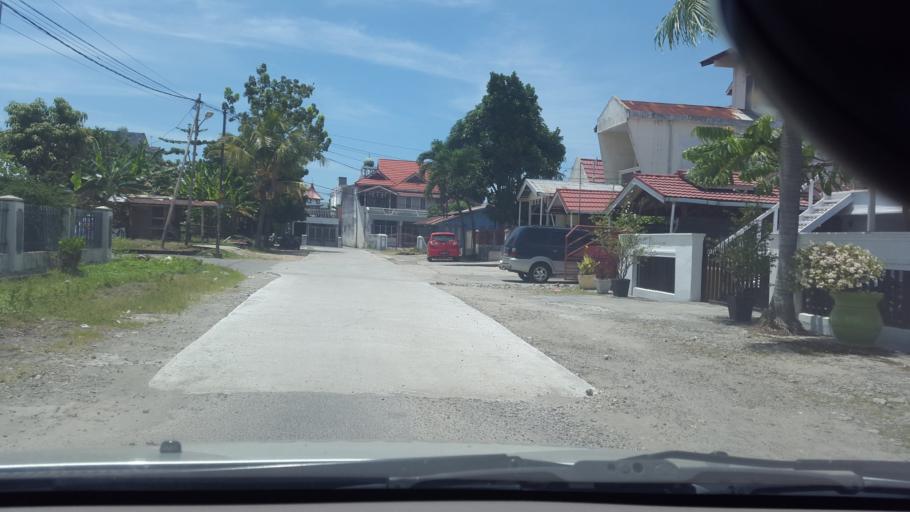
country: ID
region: West Sumatra
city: Padang
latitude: -0.9278
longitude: 100.3533
